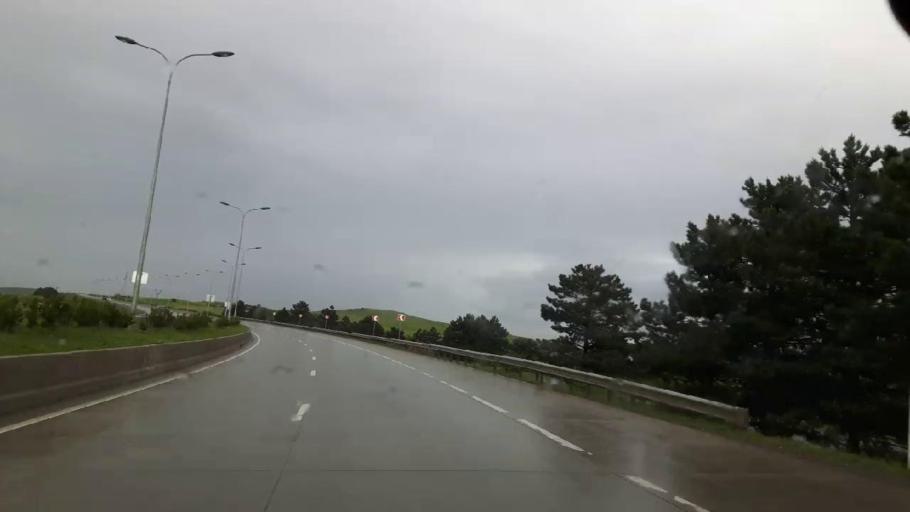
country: GE
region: Shida Kartli
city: Gori
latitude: 42.0199
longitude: 44.0017
